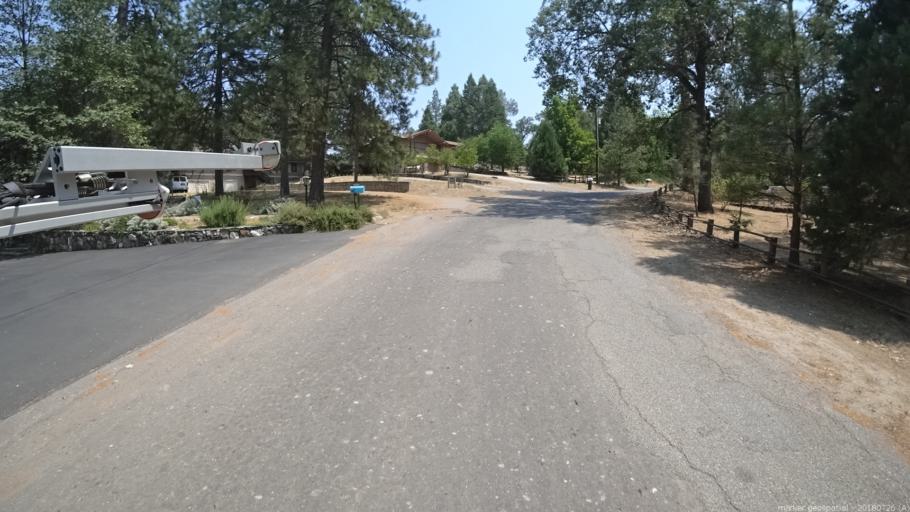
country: US
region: California
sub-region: Madera County
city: Oakhurst
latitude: 37.3268
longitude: -119.6553
